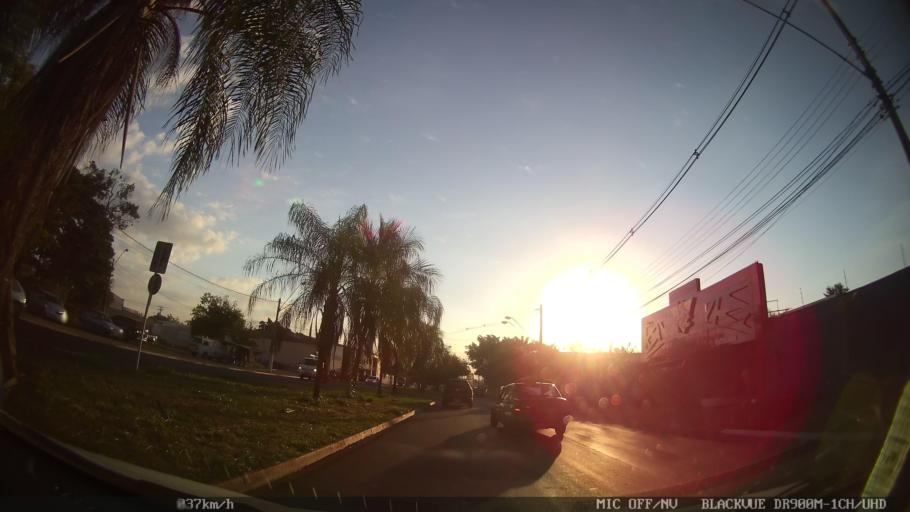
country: BR
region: Sao Paulo
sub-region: Ribeirao Preto
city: Ribeirao Preto
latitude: -21.1396
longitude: -47.7888
